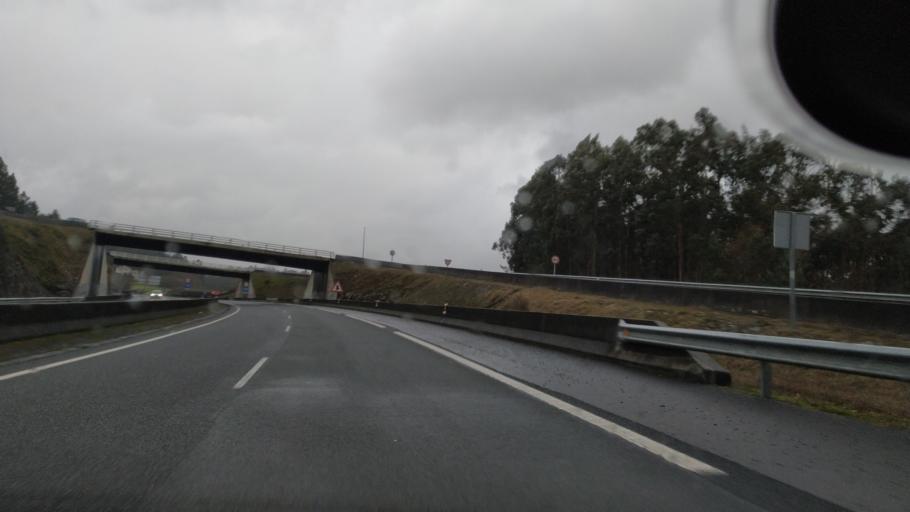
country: ES
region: Galicia
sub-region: Provincia da Coruna
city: Santiago de Compostela
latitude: 42.8361
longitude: -8.5271
